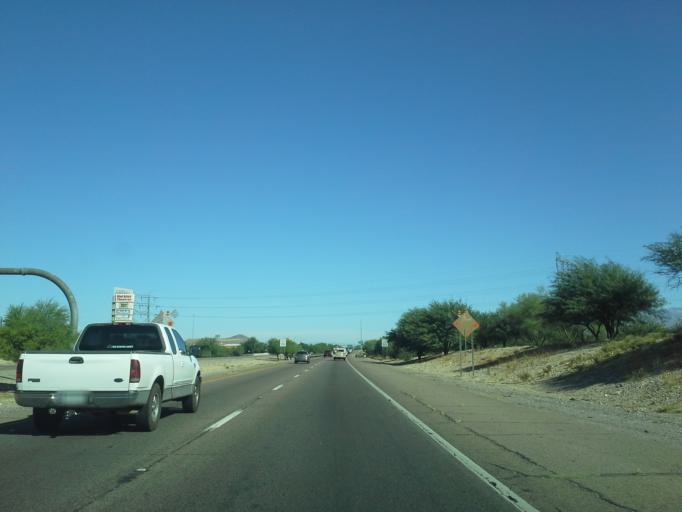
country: US
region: Arizona
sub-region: Pima County
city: Drexel Heights
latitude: 32.1526
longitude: -110.9864
